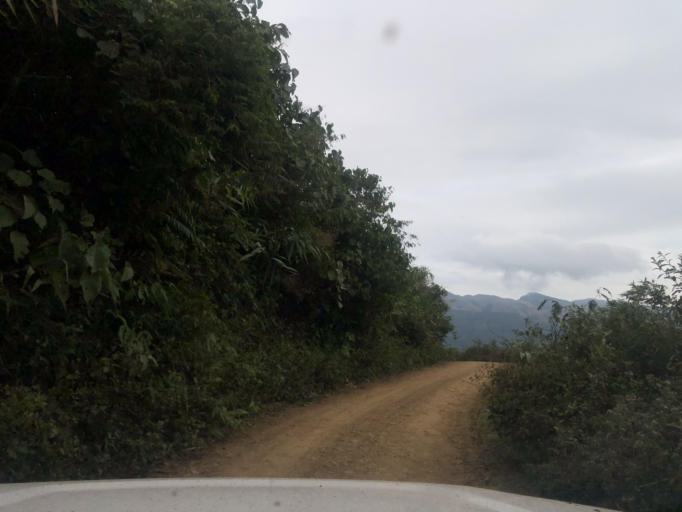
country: LA
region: Phongsali
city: Khoa
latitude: 21.2653
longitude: 102.5872
